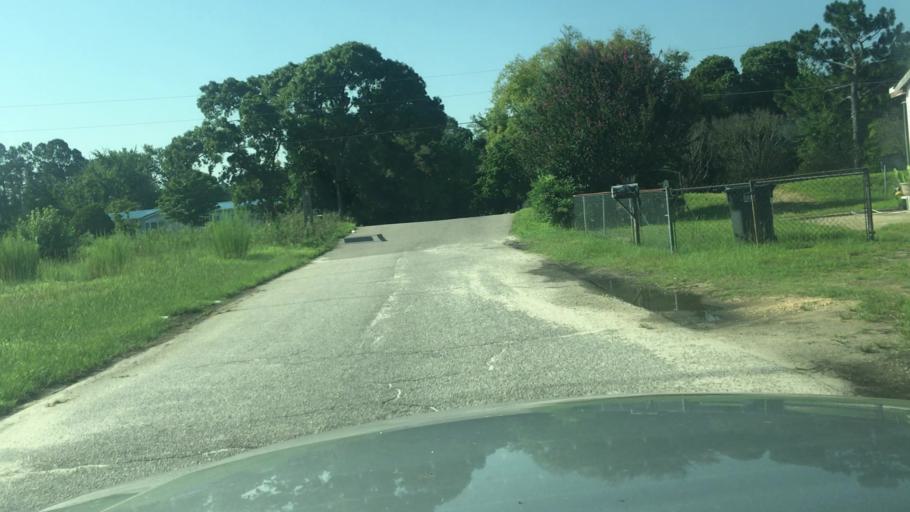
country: US
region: North Carolina
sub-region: Cumberland County
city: Spring Lake
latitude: 35.1514
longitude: -78.9143
